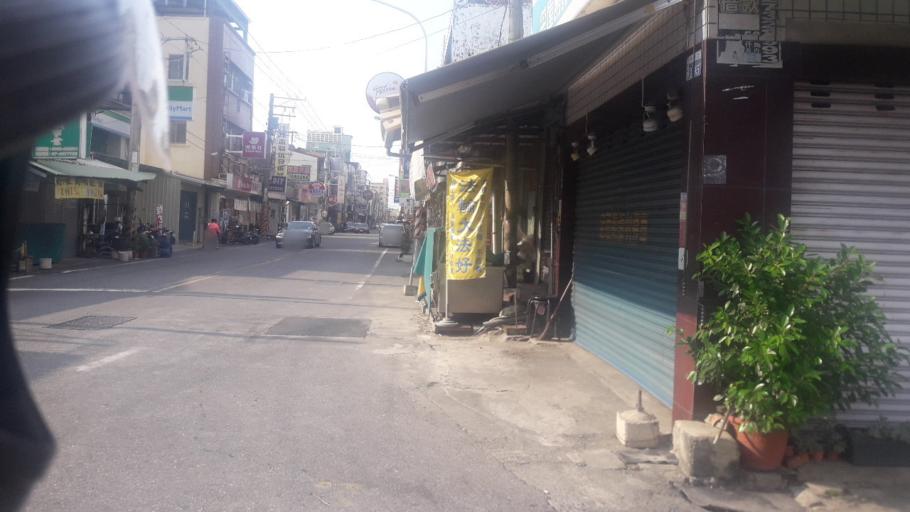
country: TW
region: Taiwan
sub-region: Tainan
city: Tainan
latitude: 22.8576
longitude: 120.2625
